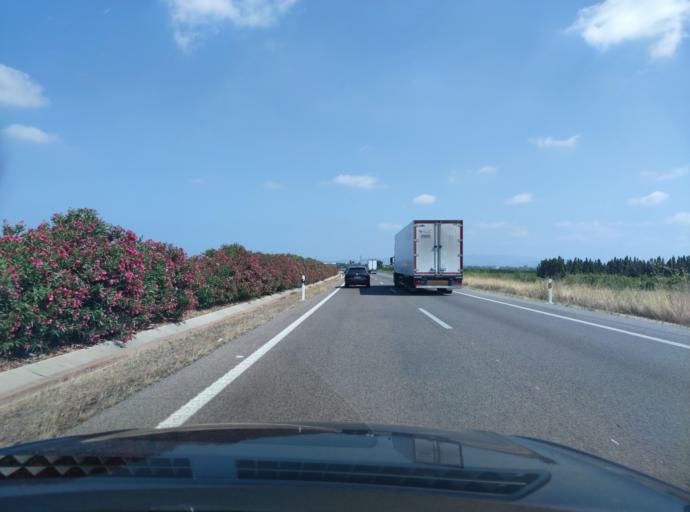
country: ES
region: Valencia
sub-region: Provincia de Castello
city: Alquerias del Nino Perdido
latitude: 39.9139
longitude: -0.1347
